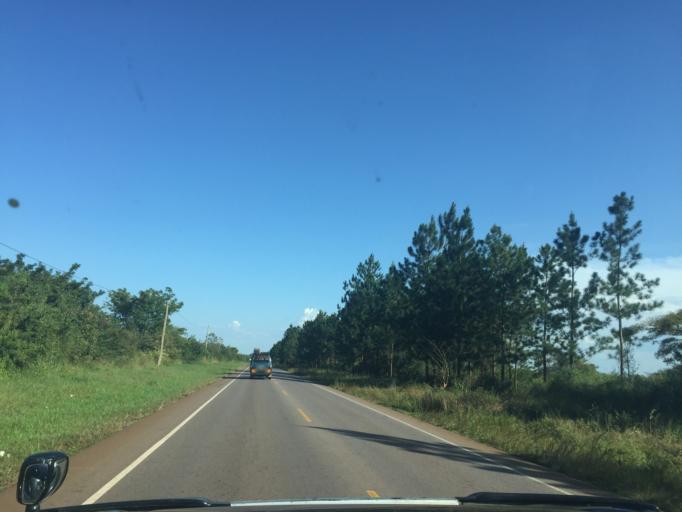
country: UG
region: Central Region
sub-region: Nakasongola District
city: Nakasongola
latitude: 1.3842
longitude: 32.3334
